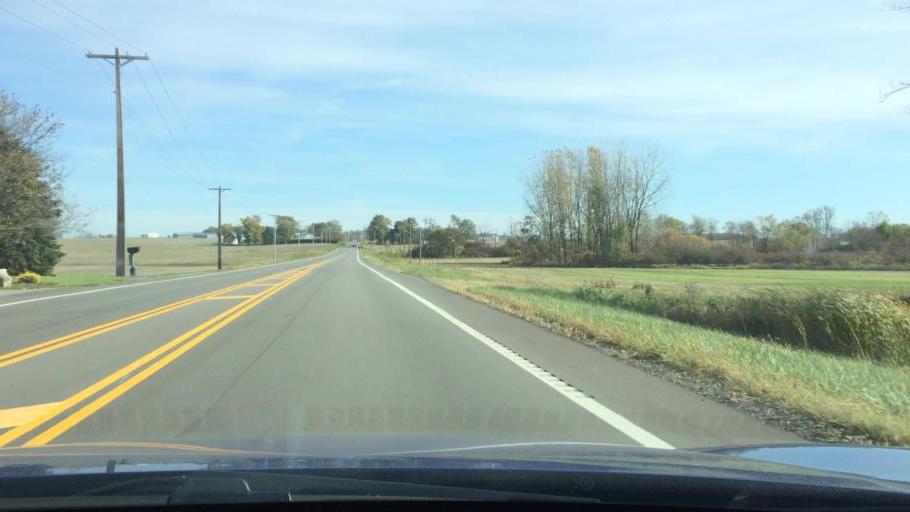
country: US
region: Ohio
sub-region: Logan County
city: Russells Point
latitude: 40.4394
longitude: -83.8896
